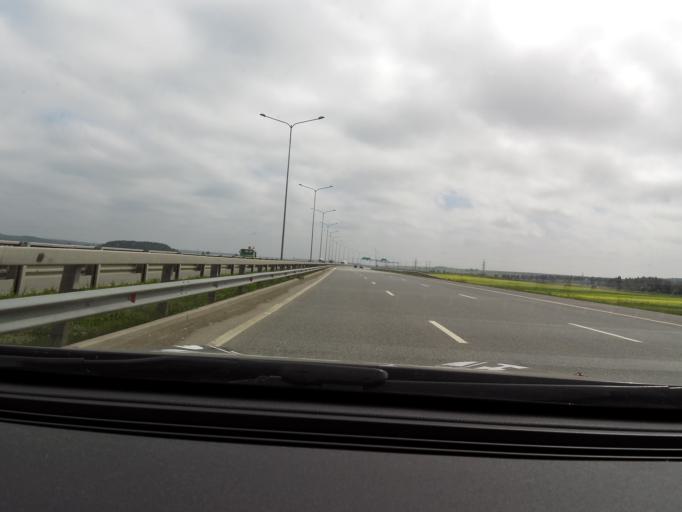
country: RU
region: Perm
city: Lobanovo
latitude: 57.8486
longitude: 56.2799
